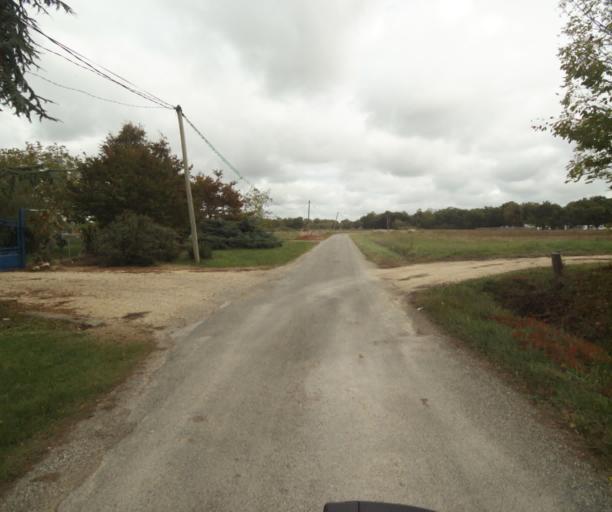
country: FR
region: Midi-Pyrenees
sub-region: Departement du Tarn-et-Garonne
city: Montech
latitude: 43.9709
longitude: 1.2480
